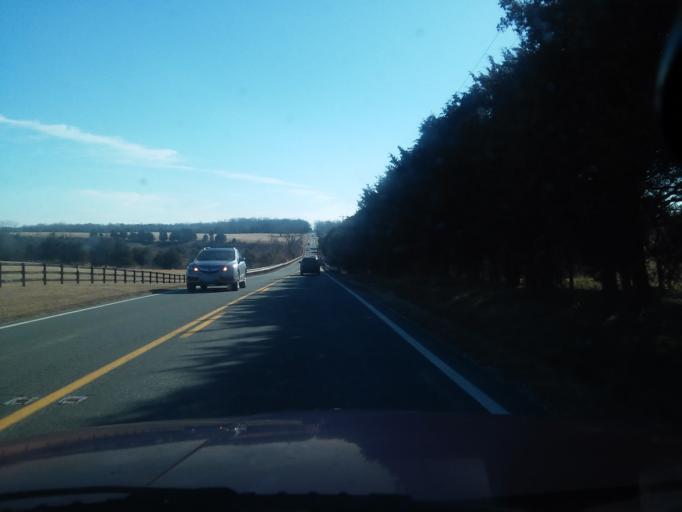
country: US
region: Virginia
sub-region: Orange County
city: Gordonsville
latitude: 38.0228
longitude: -78.1907
